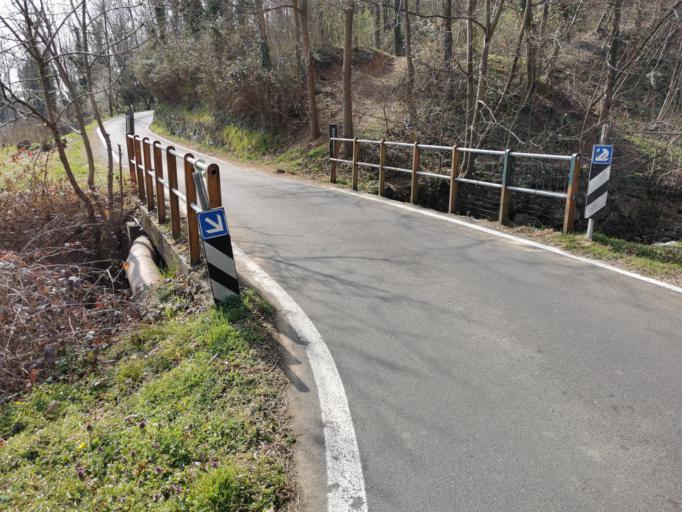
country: IT
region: Lombardy
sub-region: Provincia di Como
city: Alserio
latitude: 45.7929
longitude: 9.2057
